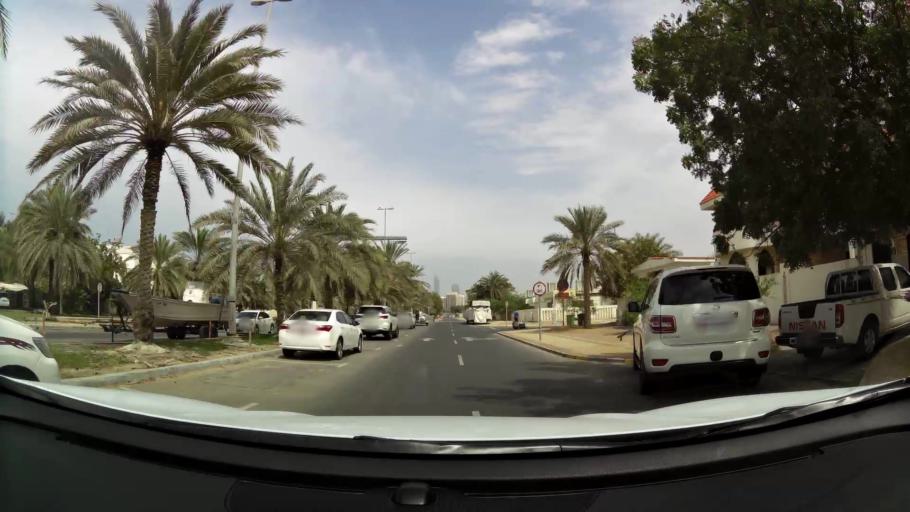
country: AE
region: Abu Dhabi
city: Abu Dhabi
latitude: 24.4594
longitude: 54.3367
